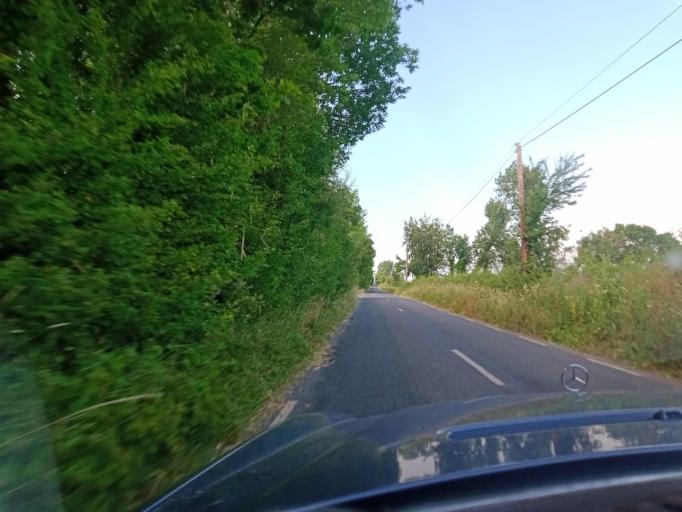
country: IE
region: Leinster
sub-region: Kilkenny
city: Callan
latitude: 52.4929
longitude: -7.3200
